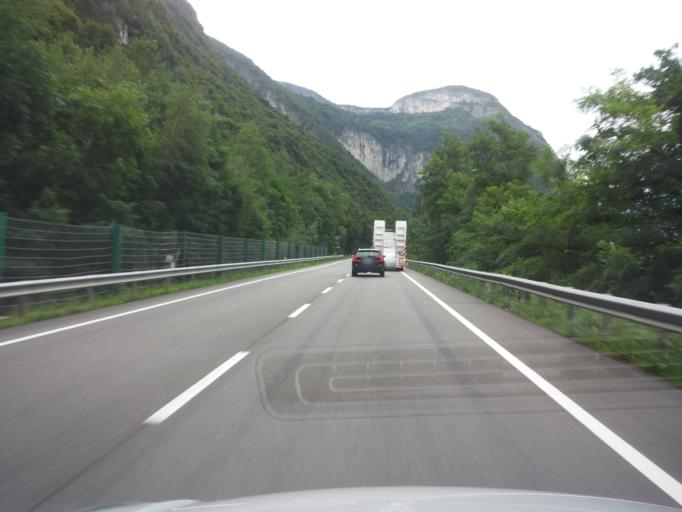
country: IT
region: Trentino-Alto Adige
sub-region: Provincia di Trento
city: Rovere della Luna
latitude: 46.2322
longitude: 11.1782
